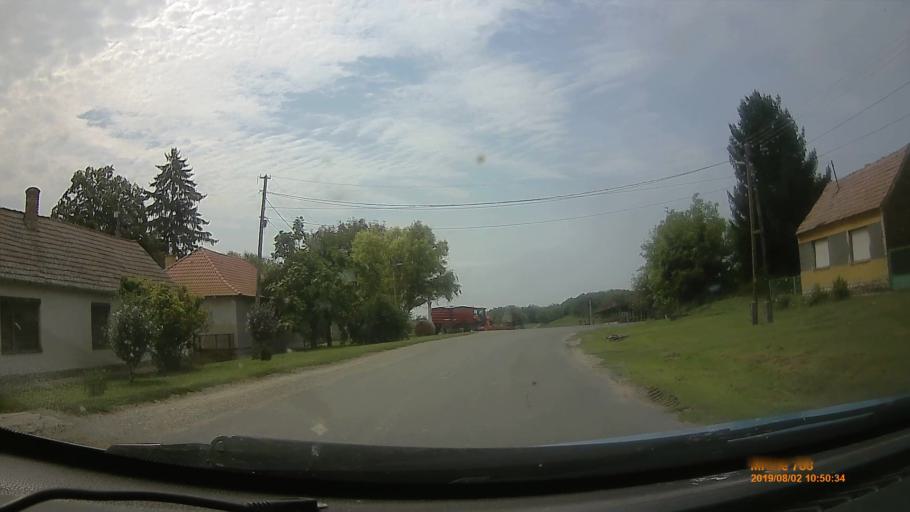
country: HU
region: Baranya
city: Buekkoesd
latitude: 46.0852
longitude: 17.9765
